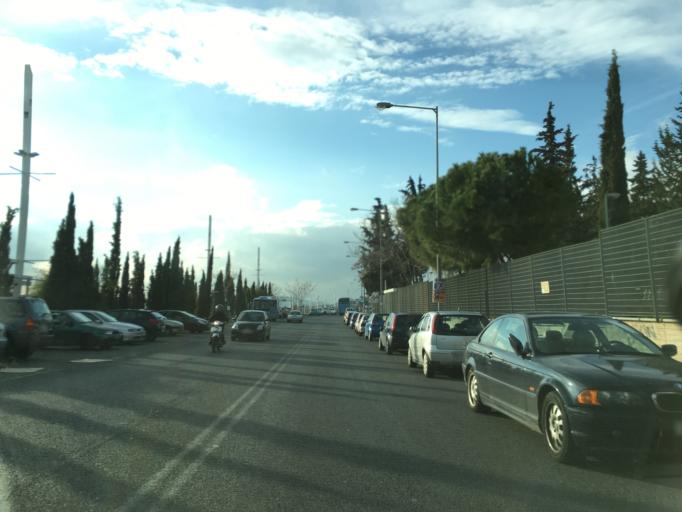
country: GR
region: Attica
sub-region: Nomarchia Athinas
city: Marousi
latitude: 38.0422
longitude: 23.7853
